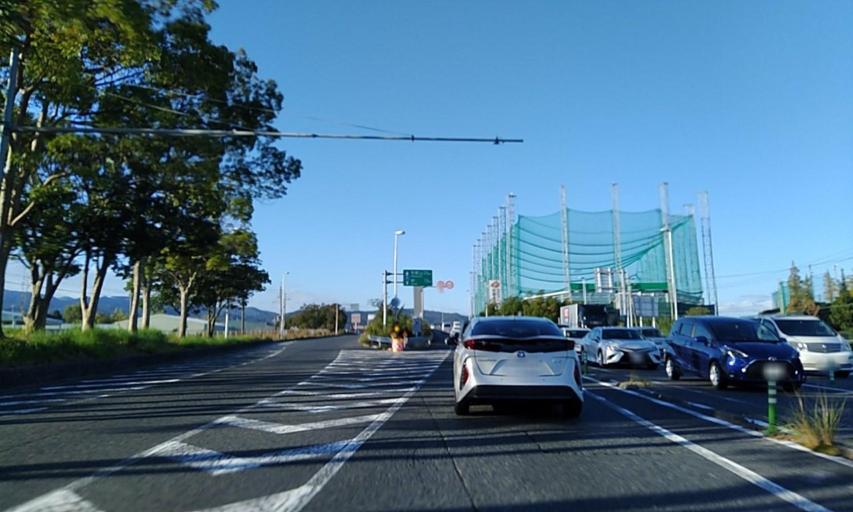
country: JP
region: Wakayama
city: Iwade
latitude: 34.3544
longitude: 135.2616
